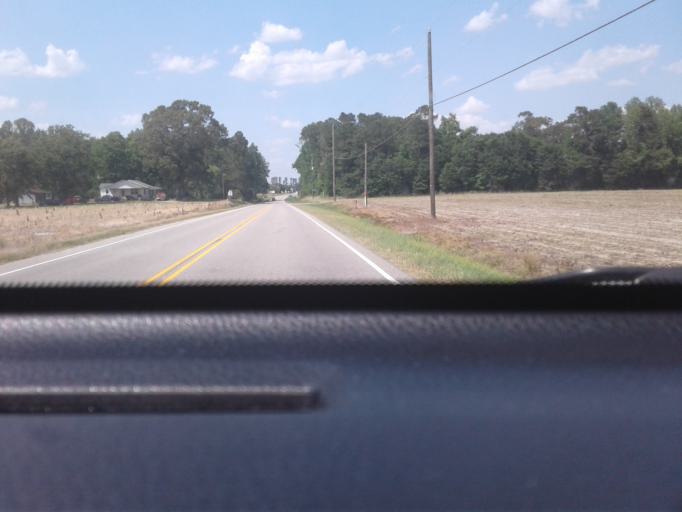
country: US
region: North Carolina
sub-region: Cumberland County
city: Eastover
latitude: 35.1414
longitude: -78.7428
